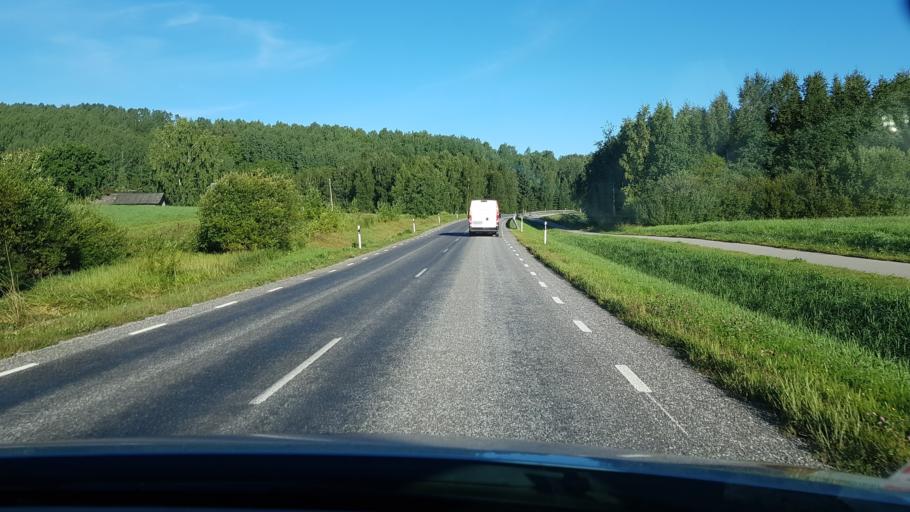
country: EE
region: Vorumaa
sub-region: Antsla vald
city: Vana-Antsla
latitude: 58.0423
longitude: 26.5509
